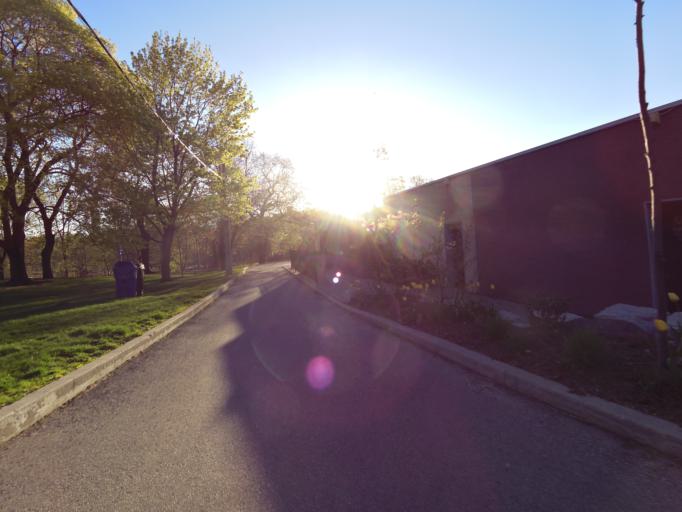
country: CA
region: Ontario
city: Toronto
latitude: 43.6676
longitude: -79.3553
